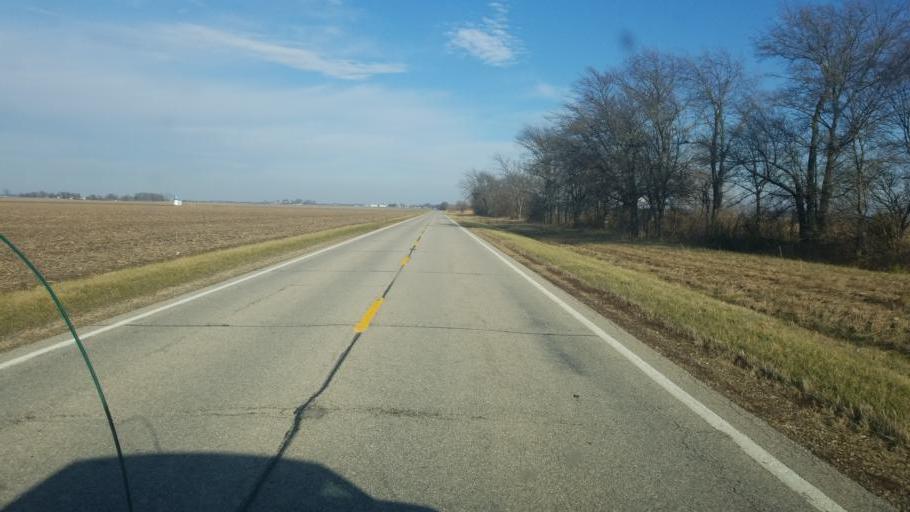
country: US
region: Illinois
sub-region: Edwards County
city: Grayville
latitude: 38.3308
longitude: -87.9040
